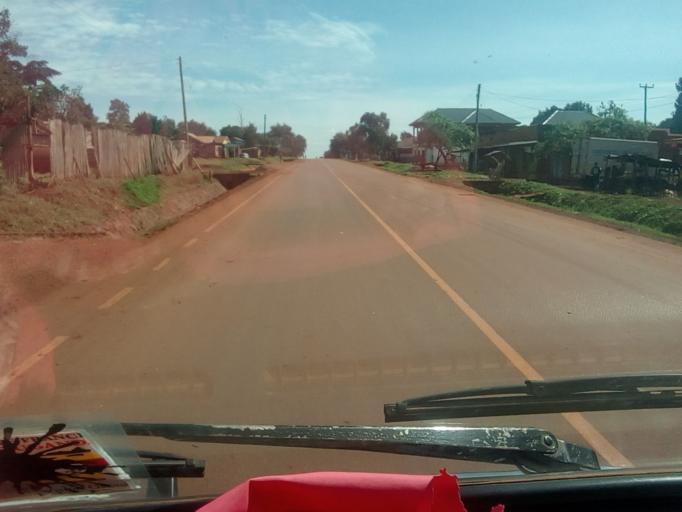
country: UG
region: Eastern Region
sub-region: Jinja District
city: Bugembe
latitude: 0.4980
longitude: 33.2265
